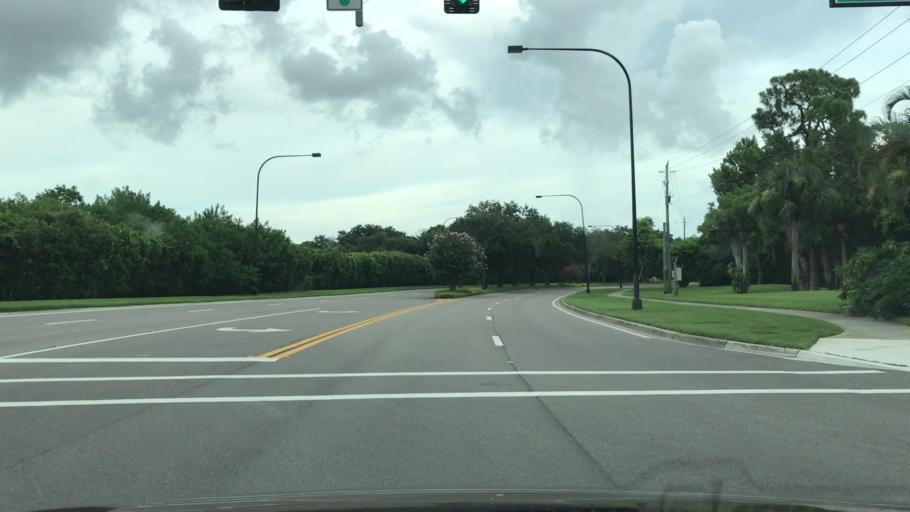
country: US
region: Florida
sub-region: Sarasota County
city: Vamo
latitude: 27.2367
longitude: -82.4891
